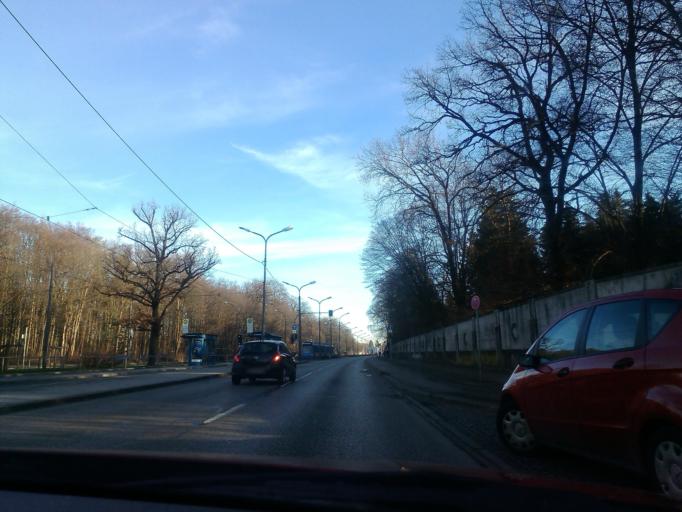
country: DE
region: Bavaria
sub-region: Upper Bavaria
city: Pasing
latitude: 48.1653
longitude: 11.4940
